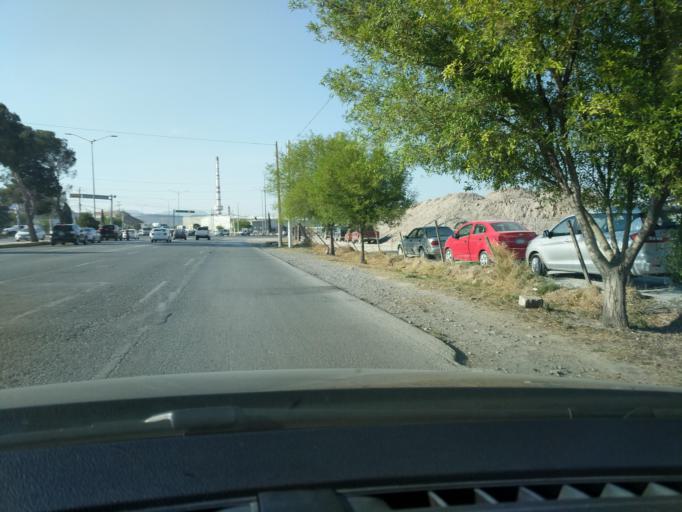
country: MX
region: Coahuila
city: Saltillo
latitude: 25.4777
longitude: -100.9835
